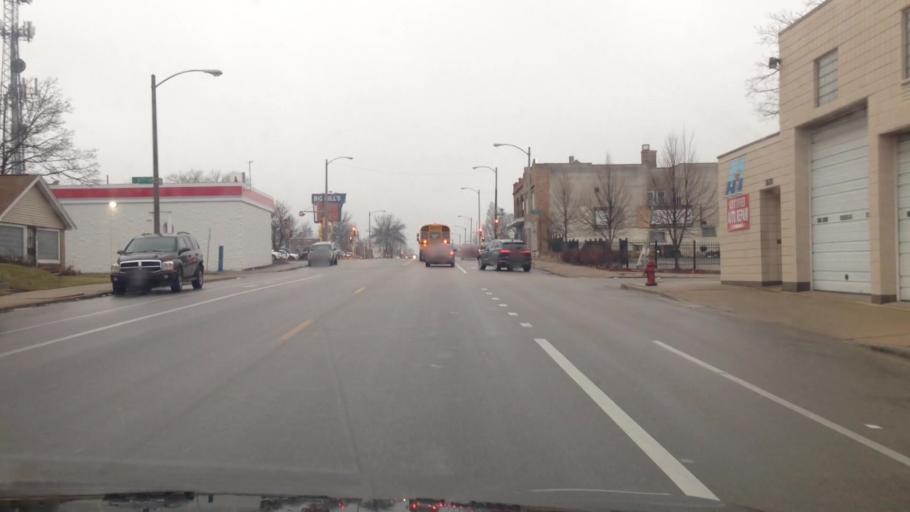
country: US
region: Wisconsin
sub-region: Milwaukee County
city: Wauwatosa
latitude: 43.0681
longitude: -87.9838
